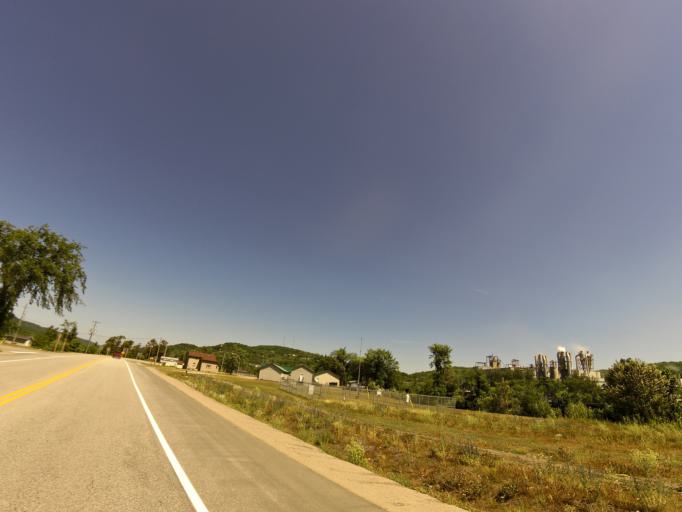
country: CA
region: Quebec
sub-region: Abitibi-Temiscamingue
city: Temiscaming
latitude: 46.7092
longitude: -79.1010
